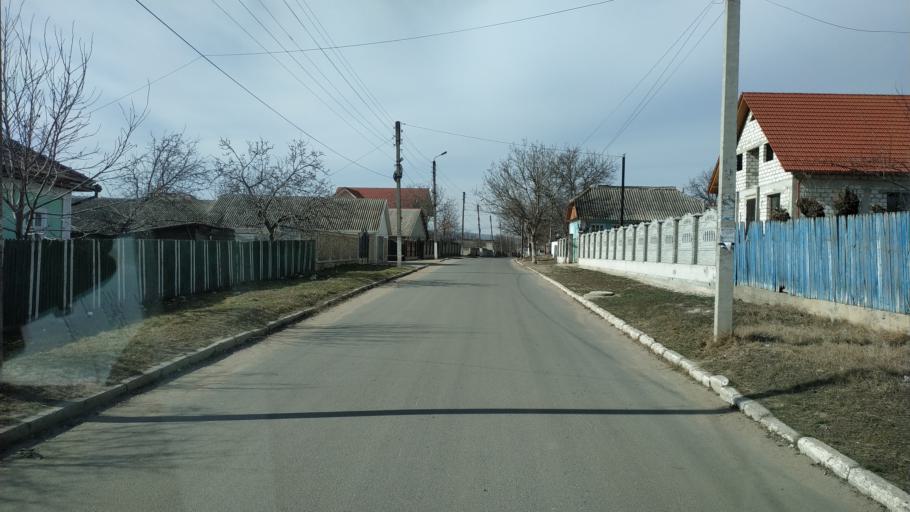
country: MD
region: Straseni
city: Straseni
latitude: 47.0957
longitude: 28.6592
